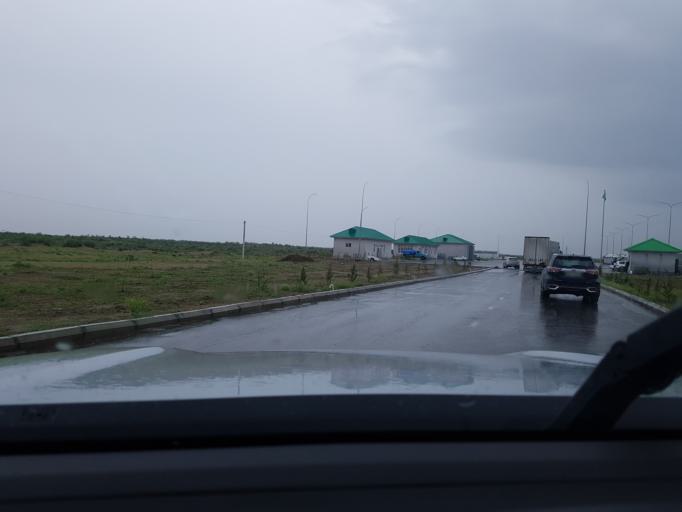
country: TM
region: Lebap
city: Farap
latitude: 39.2075
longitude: 63.6986
